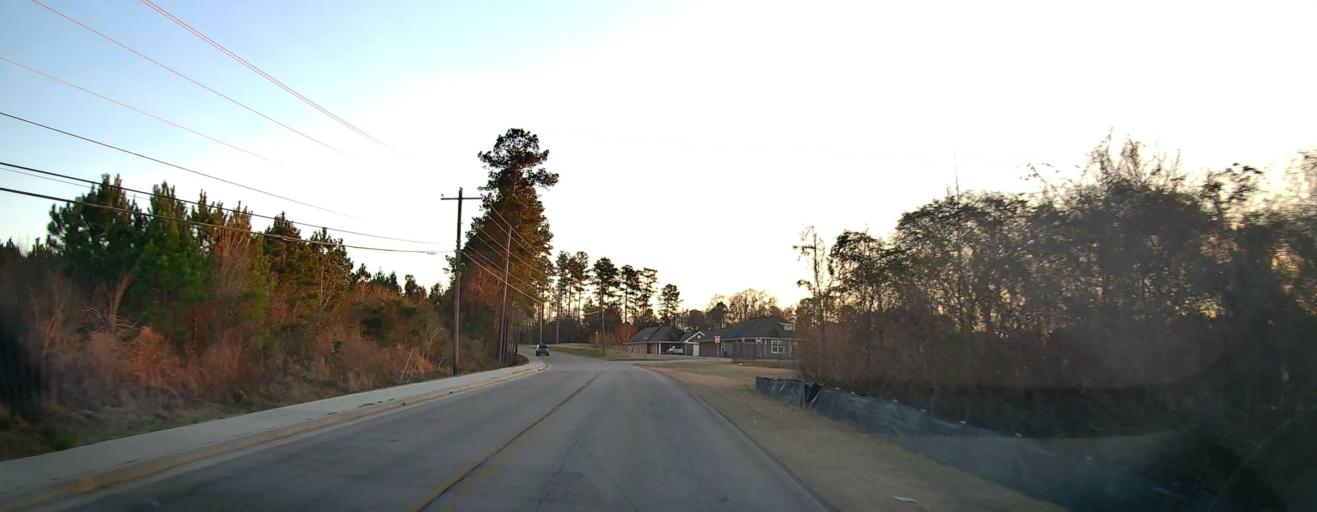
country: US
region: Georgia
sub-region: Troup County
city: La Grange
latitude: 33.0262
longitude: -85.0046
